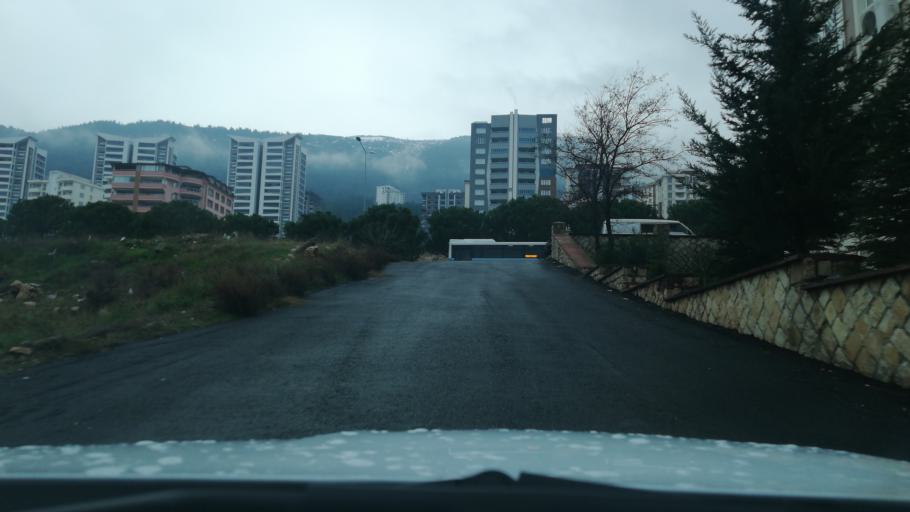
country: TR
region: Kahramanmaras
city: Kahramanmaras
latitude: 37.5957
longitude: 36.8496
